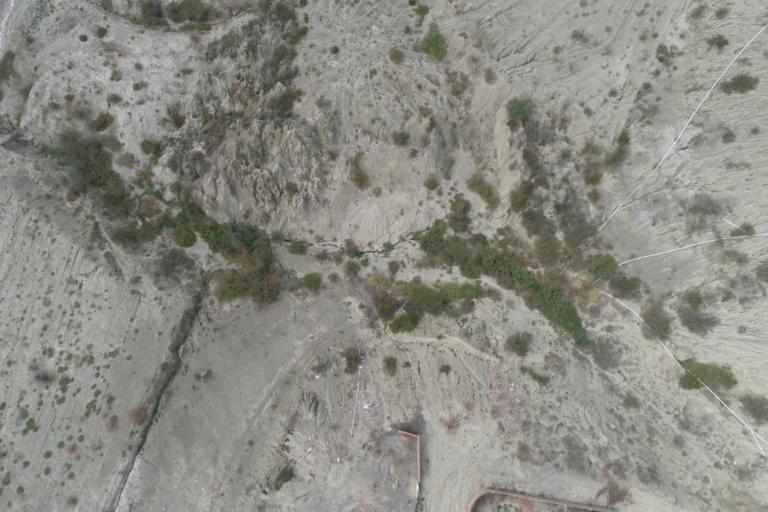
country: BO
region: La Paz
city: La Paz
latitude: -16.5994
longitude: -68.0676
